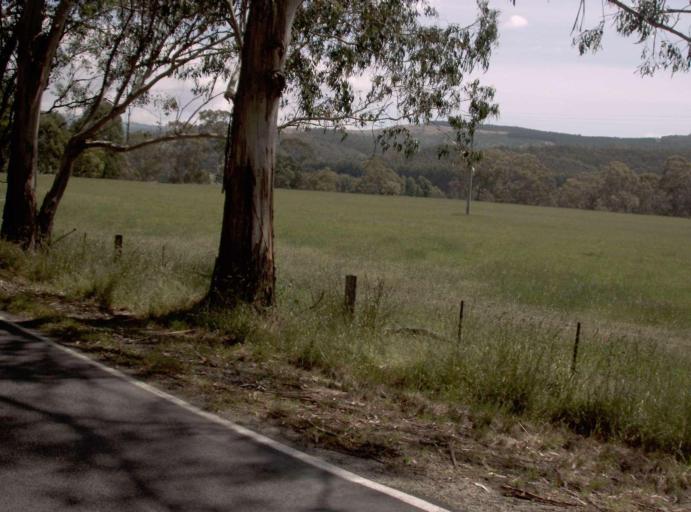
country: AU
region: Victoria
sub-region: Latrobe
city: Traralgon
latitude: -38.2900
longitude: 146.5397
